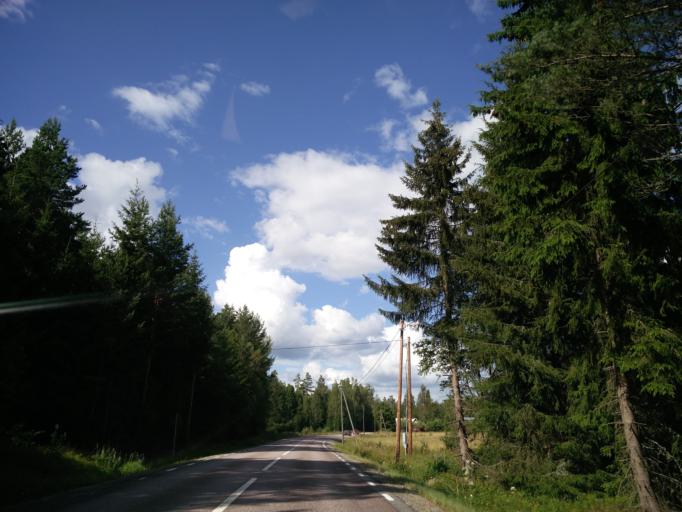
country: SE
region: Vaermland
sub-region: Sunne Kommun
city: Sunne
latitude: 59.6604
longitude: 12.9596
